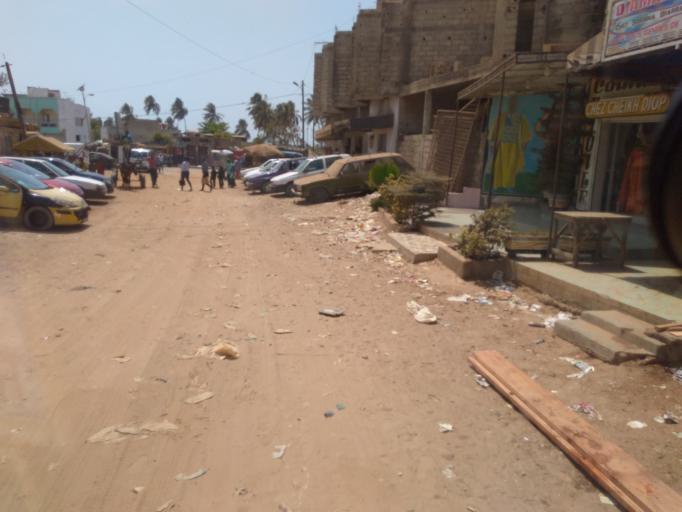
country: SN
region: Dakar
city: Pikine
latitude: 14.7903
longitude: -17.3413
